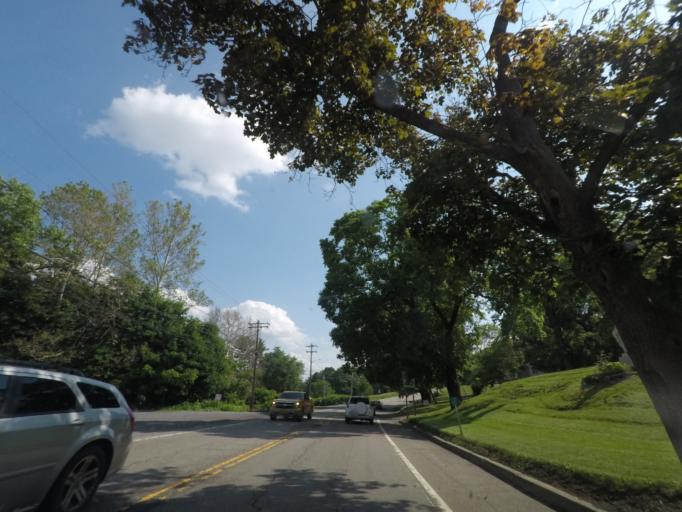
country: US
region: New York
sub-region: Ulster County
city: Marlboro
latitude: 41.6012
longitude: -73.9726
